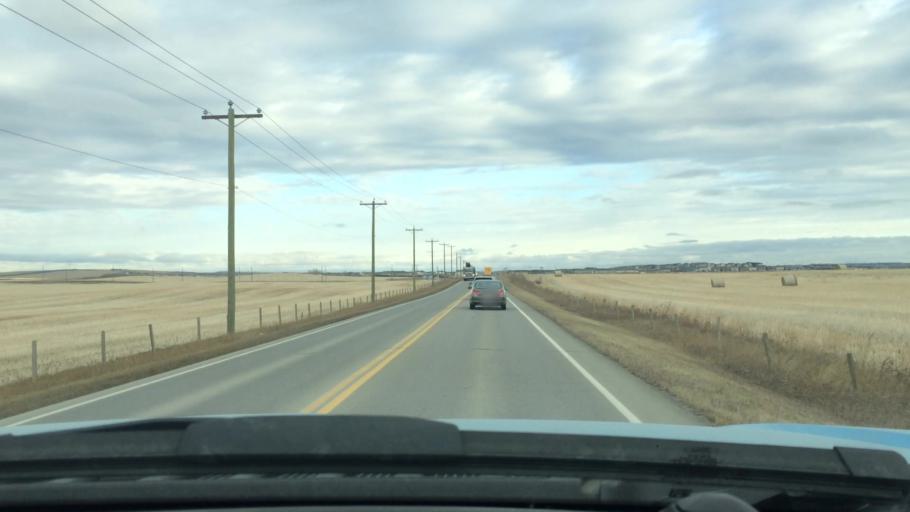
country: CA
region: Alberta
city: Airdrie
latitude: 51.2355
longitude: -114.0249
